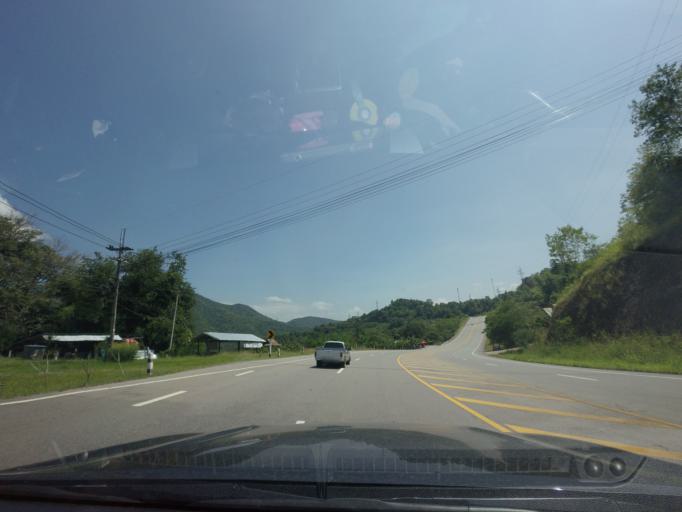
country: TH
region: Phetchabun
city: Lom Sak
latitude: 16.7796
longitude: 101.1081
